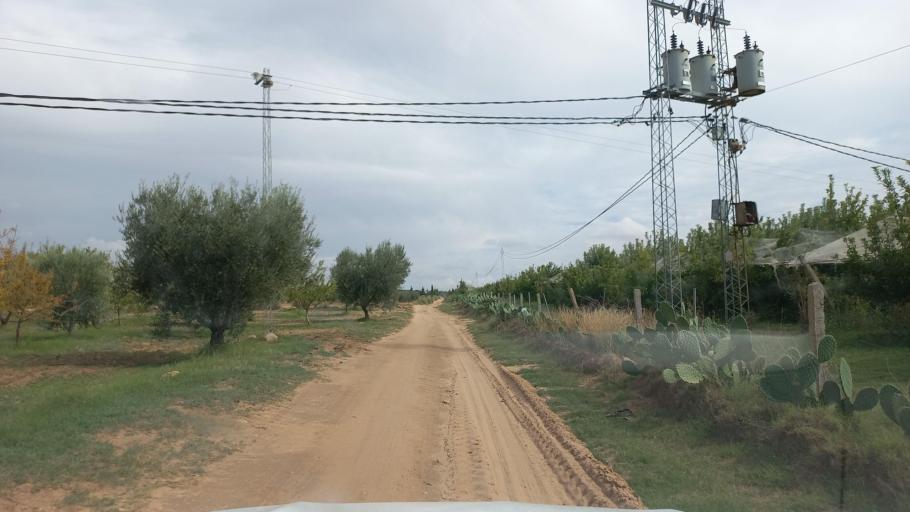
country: TN
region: Al Qasrayn
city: Sbiba
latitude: 35.3060
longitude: 9.1109
